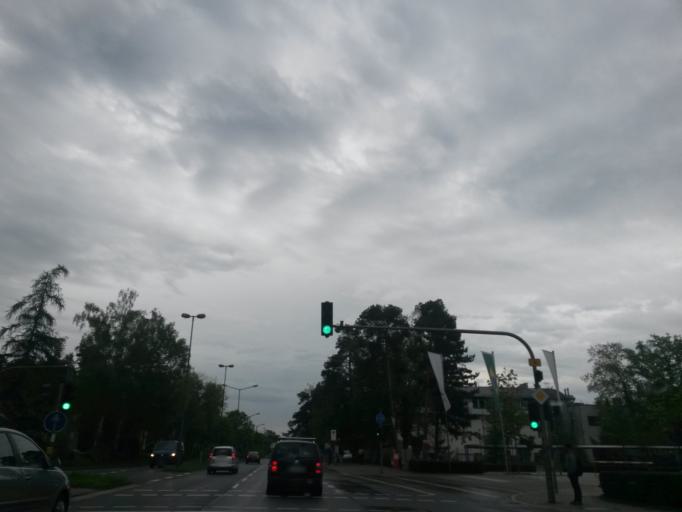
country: DE
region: Bavaria
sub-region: Regierungsbezirk Mittelfranken
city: Erlangen
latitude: 49.5764
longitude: 11.0093
